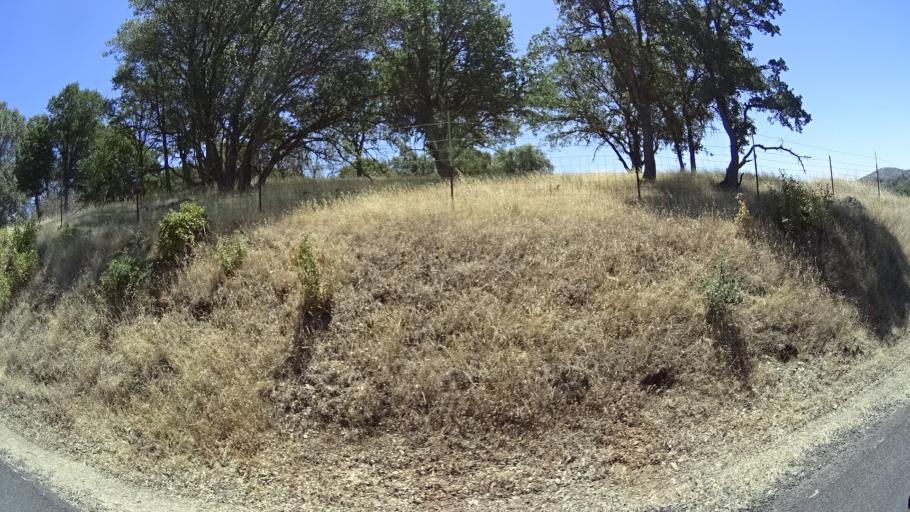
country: US
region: California
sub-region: Calaveras County
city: Copperopolis
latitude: 37.9802
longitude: -120.6933
